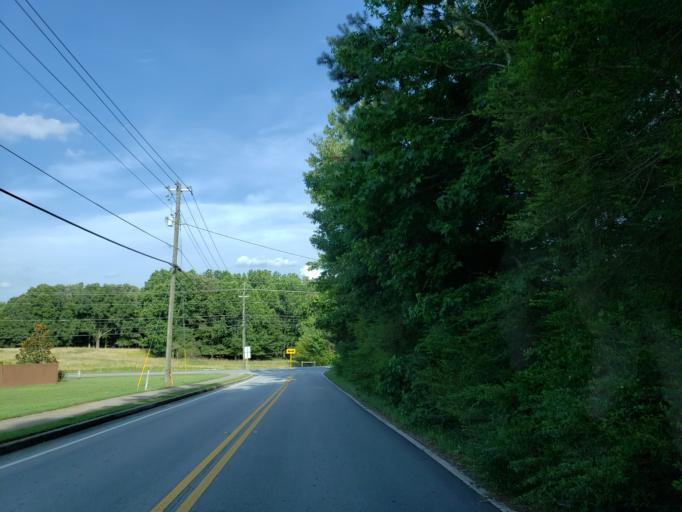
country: US
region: Georgia
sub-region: Cobb County
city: Powder Springs
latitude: 33.9111
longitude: -84.7070
